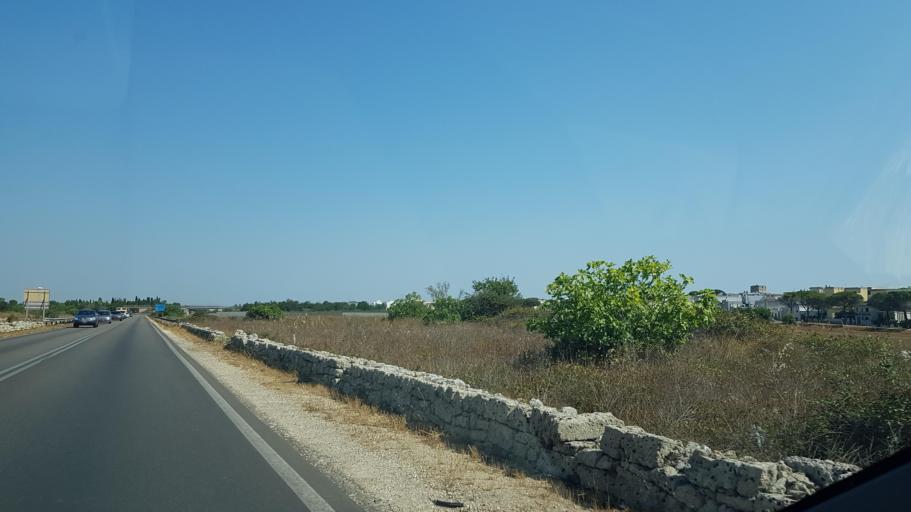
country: IT
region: Apulia
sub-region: Provincia di Lecce
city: Nociglia
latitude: 40.0327
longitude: 18.3238
